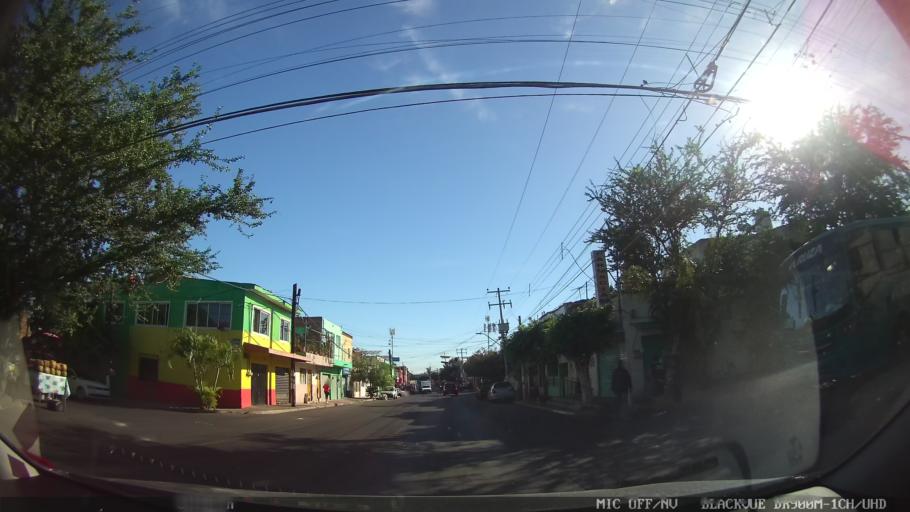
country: MX
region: Jalisco
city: Tlaquepaque
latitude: 20.6873
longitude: -103.2788
